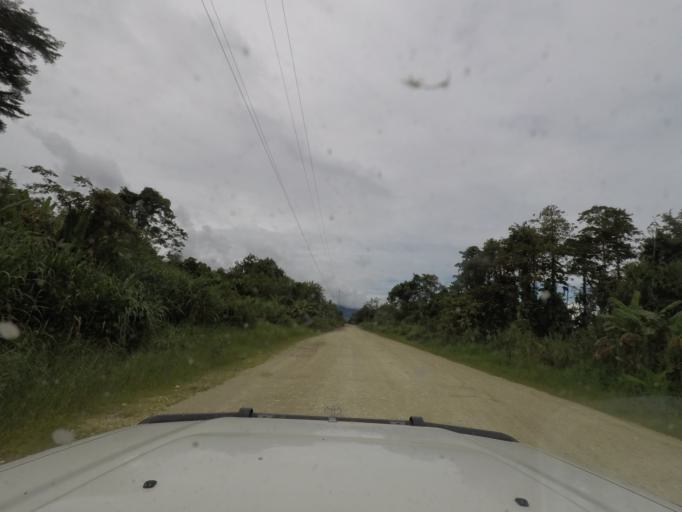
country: PG
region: Eastern Highlands
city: Goroka
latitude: -5.6887
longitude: 145.5144
